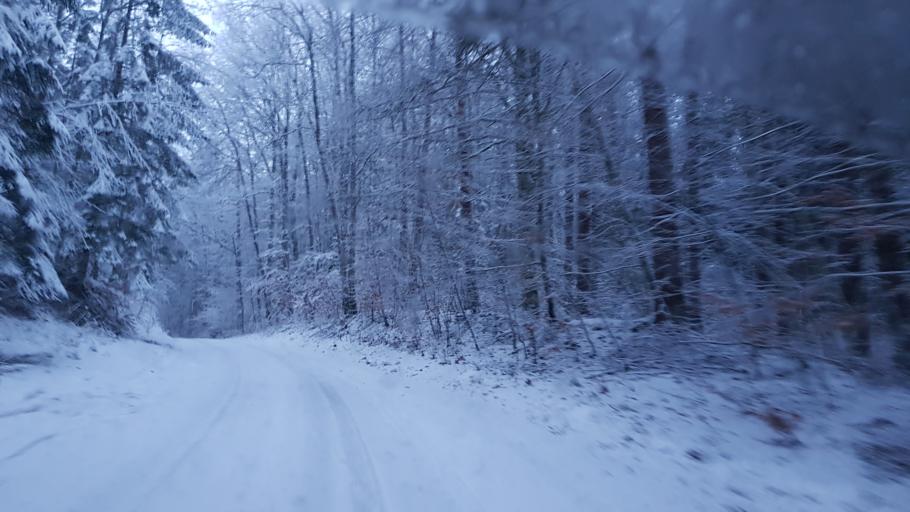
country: PL
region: West Pomeranian Voivodeship
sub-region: Powiat koszalinski
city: Sianow
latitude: 54.1669
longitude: 16.4718
